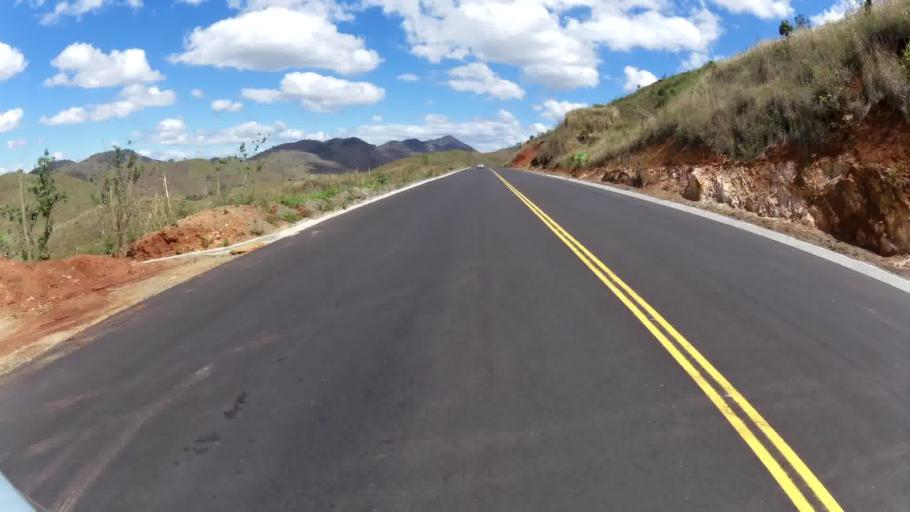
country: BR
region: Rio de Janeiro
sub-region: Itaperuna
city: Itaperuna
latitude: -21.2870
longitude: -41.7994
